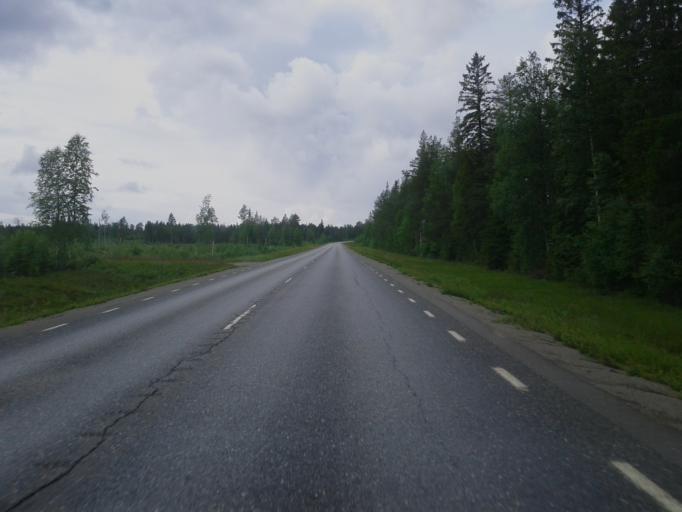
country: SE
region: Vaesterbotten
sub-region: Norsjo Kommun
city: Norsjoe
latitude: 64.9872
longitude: 19.4021
